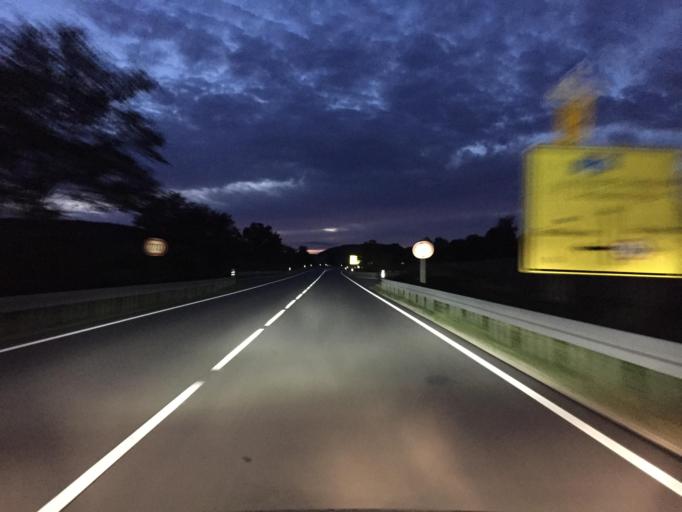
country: DE
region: Baden-Wuerttemberg
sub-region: Freiburg Region
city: Blumberg
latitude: 47.8611
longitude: 8.5472
